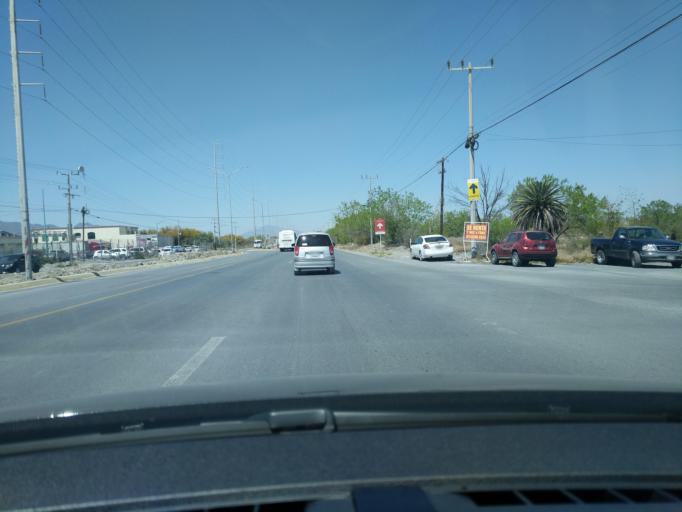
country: MX
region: Nuevo Leon
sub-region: Salinas Victoria
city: Emiliano Zapata
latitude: 25.9046
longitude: -100.2643
